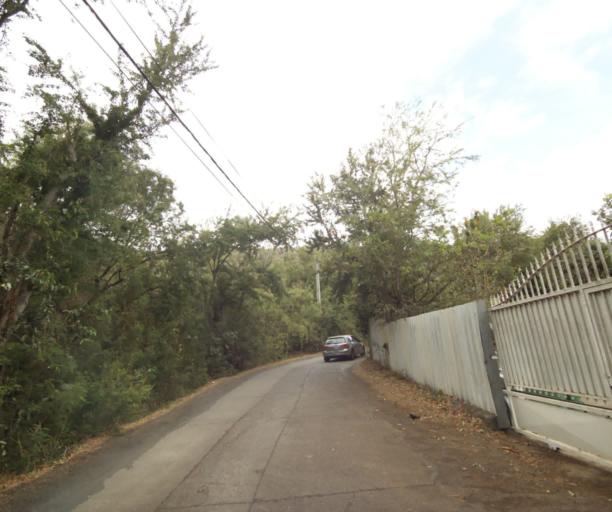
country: RE
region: Reunion
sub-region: Reunion
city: Saint-Paul
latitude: -21.0012
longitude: 55.3015
